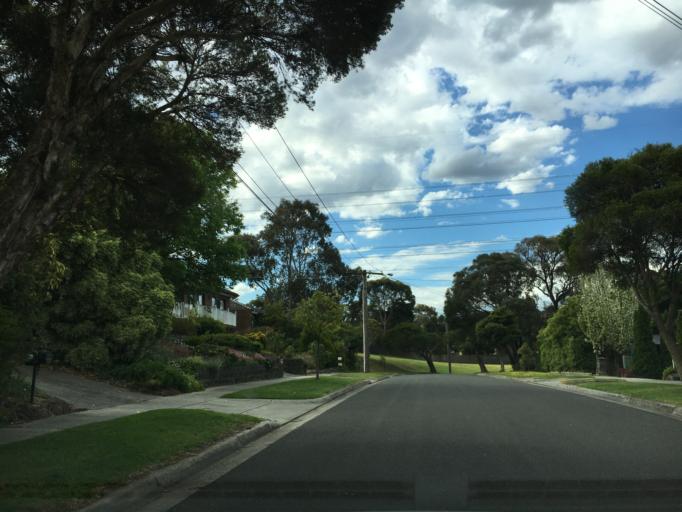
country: AU
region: Victoria
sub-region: Monash
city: Notting Hill
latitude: -37.8898
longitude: 145.1222
